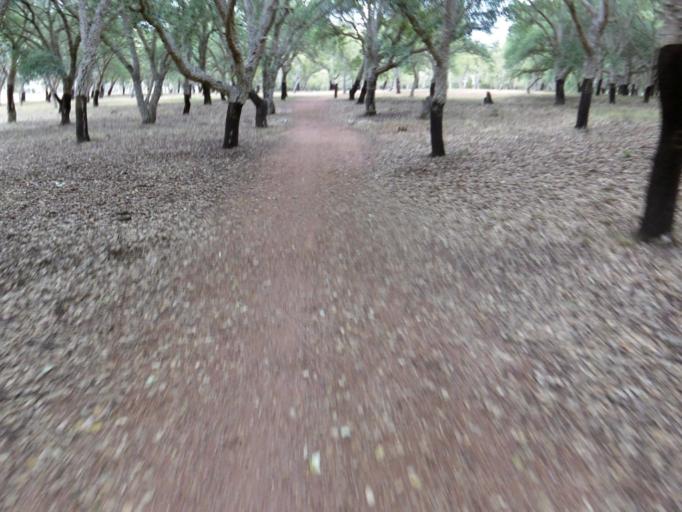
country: AU
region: Australian Capital Territory
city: Macquarie
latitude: -35.2806
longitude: 149.0806
